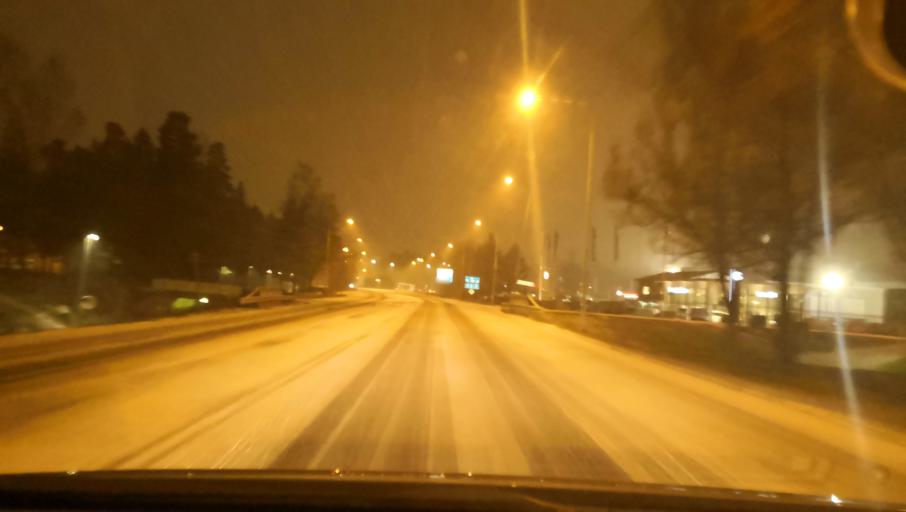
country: SE
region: Vaestmanland
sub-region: Vasteras
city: Hokasen
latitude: 59.6346
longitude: 16.5847
